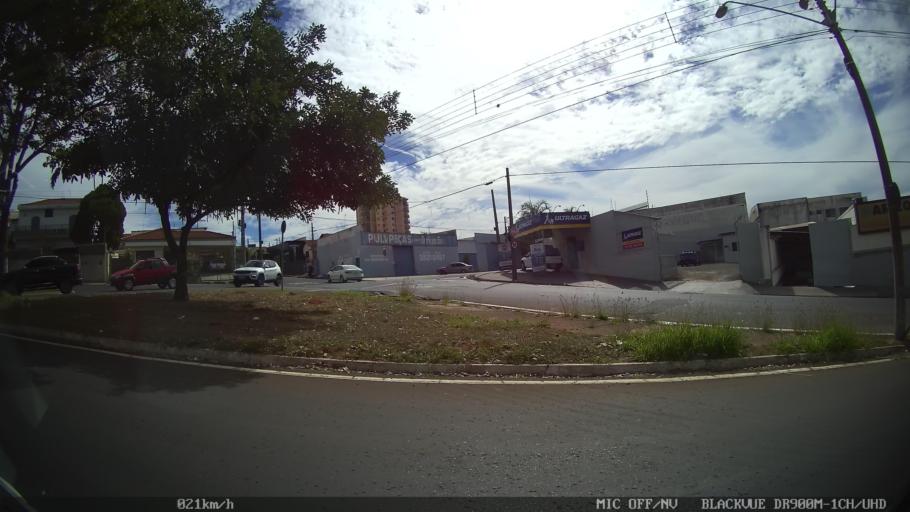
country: BR
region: Sao Paulo
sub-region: Catanduva
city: Catanduva
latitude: -21.1499
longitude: -48.9787
